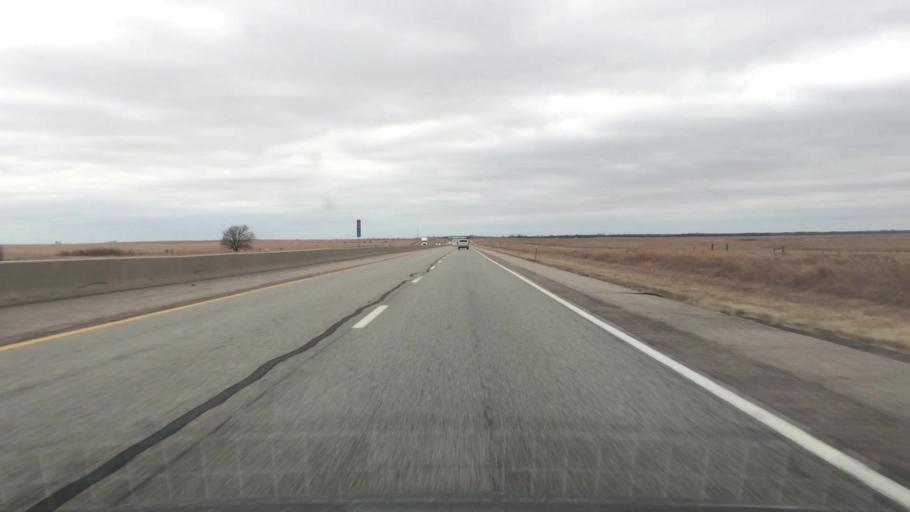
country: US
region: Kansas
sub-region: Butler County
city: El Dorado
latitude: 37.9981
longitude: -96.6930
